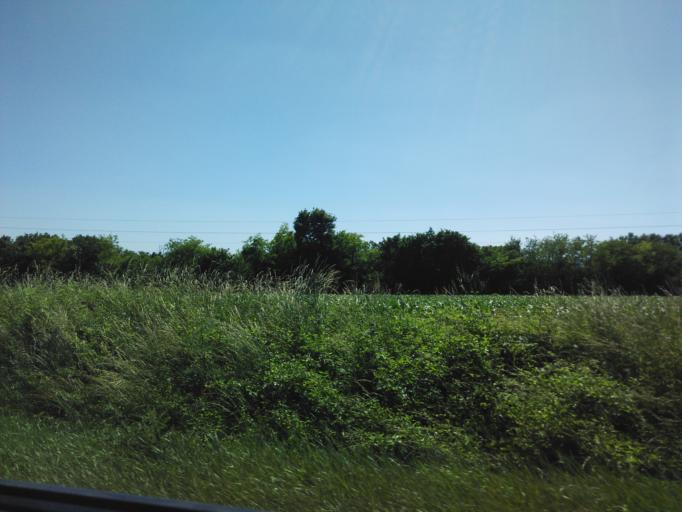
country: HU
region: Fejer
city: Kincsesbanya
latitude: 47.2795
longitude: 18.3165
